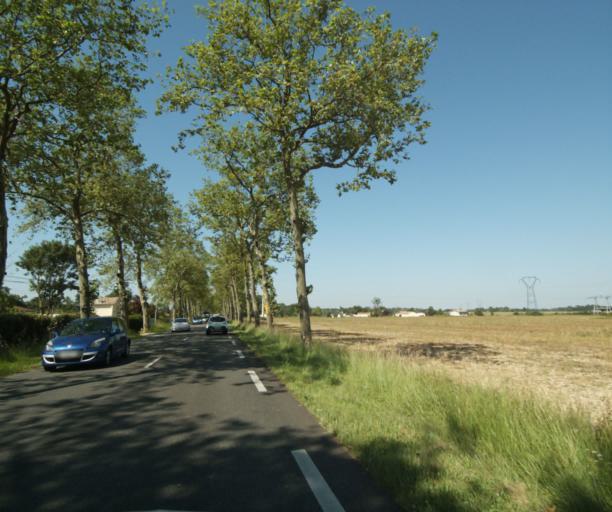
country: FR
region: Midi-Pyrenees
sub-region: Departement du Tarn-et-Garonne
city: Montbeton
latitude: 43.9809
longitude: 1.2926
